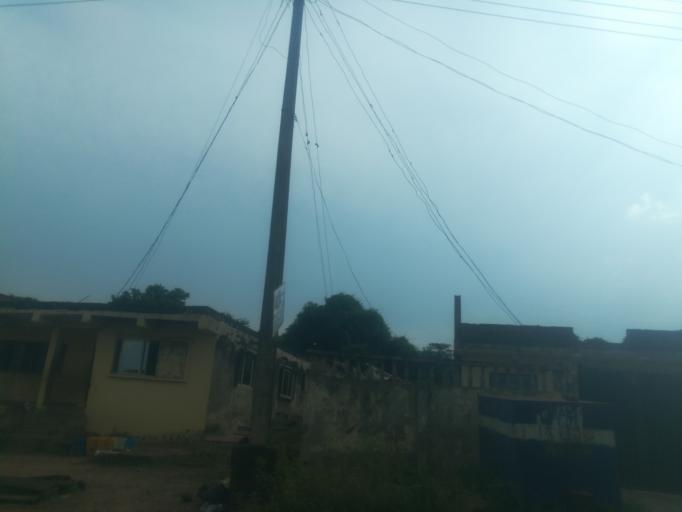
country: NG
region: Ogun
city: Abeokuta
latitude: 7.1361
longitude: 3.3007
